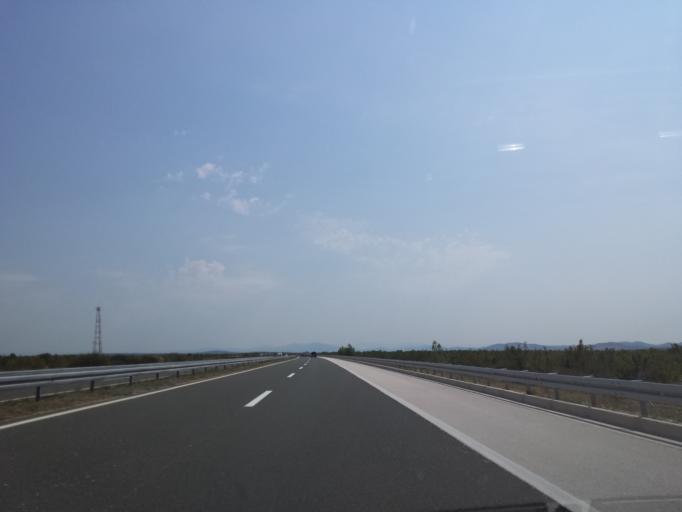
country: HR
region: Sibensko-Kniniska
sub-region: Grad Sibenik
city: Pirovac
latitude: 43.9133
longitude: 15.7489
